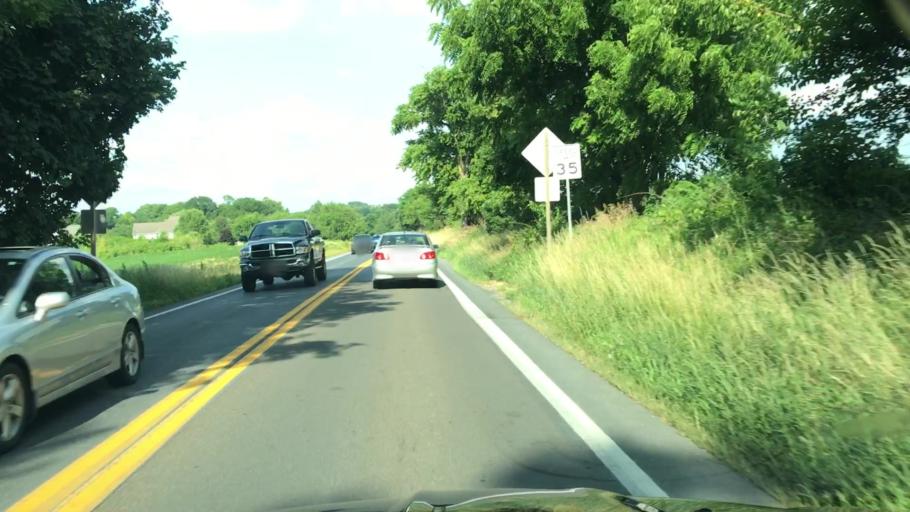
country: US
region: Pennsylvania
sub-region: York County
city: Dillsburg
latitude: 40.1607
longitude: -77.0189
